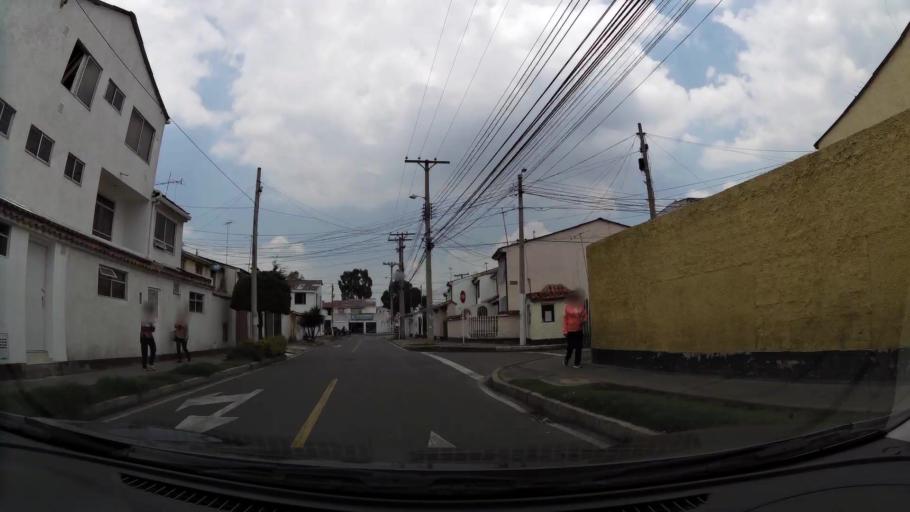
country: CO
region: Cundinamarca
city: Cota
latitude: 4.7551
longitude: -74.0487
